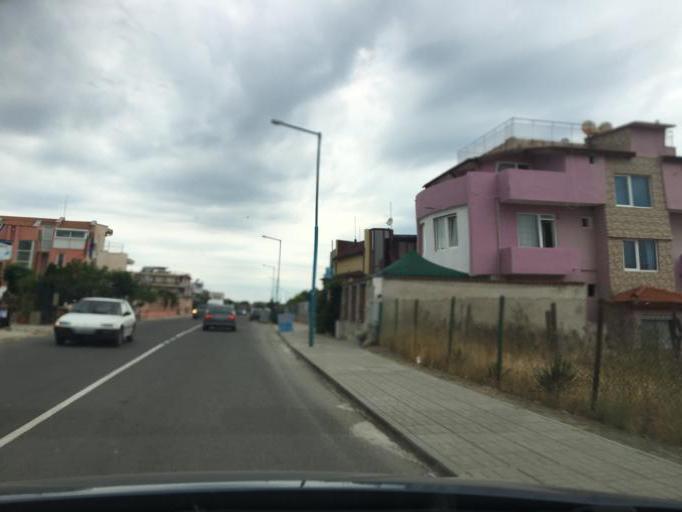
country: BG
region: Burgas
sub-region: Obshtina Sozopol
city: Sozopol
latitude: 42.4088
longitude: 27.7038
